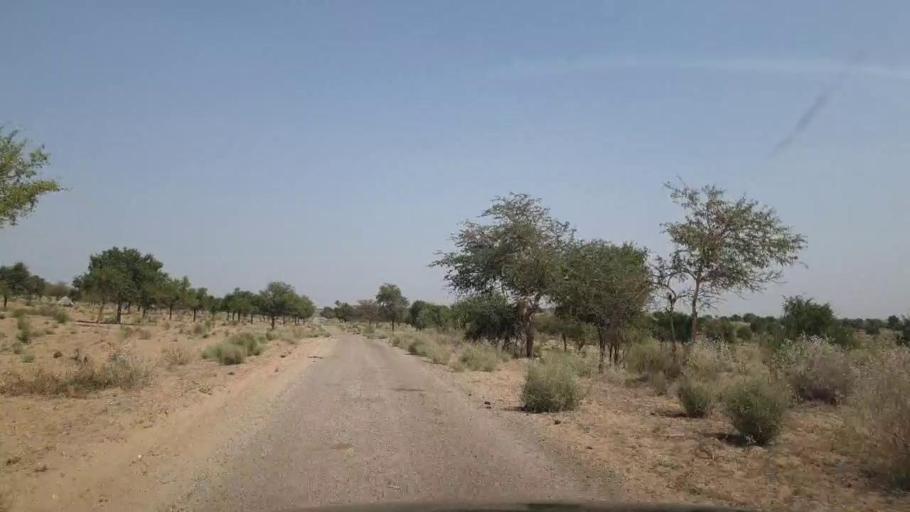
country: PK
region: Sindh
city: Islamkot
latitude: 25.0965
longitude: 70.7493
